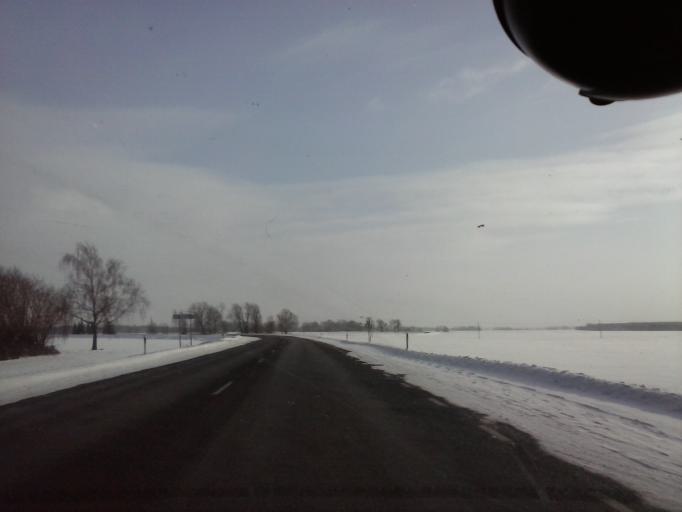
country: EE
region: Tartu
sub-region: Puhja vald
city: Puhja
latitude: 58.3343
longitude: 26.1850
